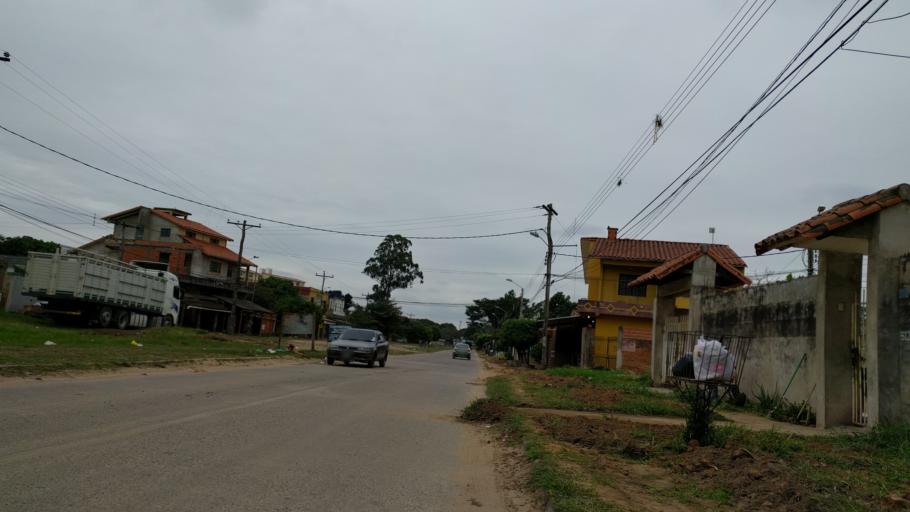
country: BO
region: Santa Cruz
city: Santa Cruz de la Sierra
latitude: -17.8065
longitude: -63.2226
